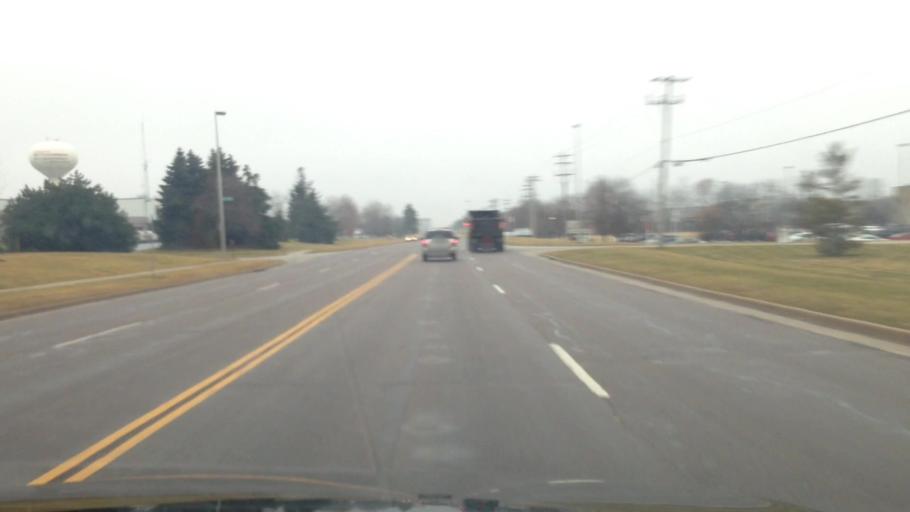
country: US
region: Wisconsin
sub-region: Washington County
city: Germantown
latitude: 43.2315
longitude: -88.1428
